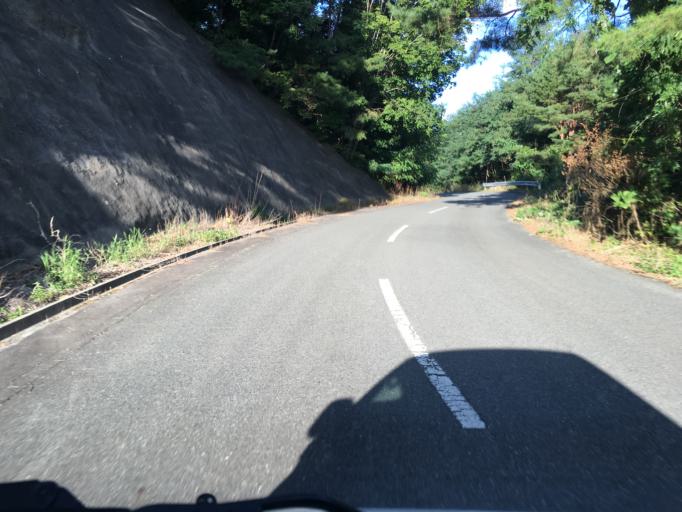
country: JP
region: Yamagata
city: Yonezawa
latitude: 37.8655
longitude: 140.1757
